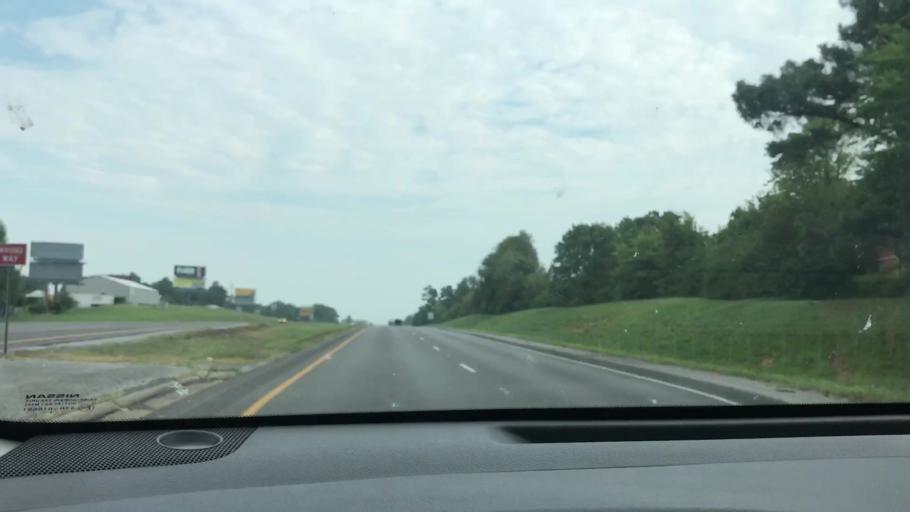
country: US
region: Kentucky
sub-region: Calloway County
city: Murray
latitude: 36.6773
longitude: -88.3025
